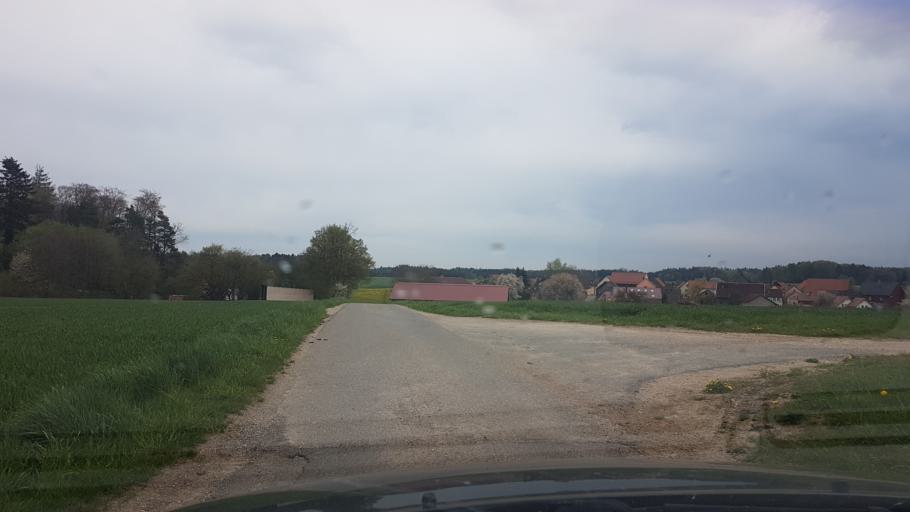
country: DE
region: Bavaria
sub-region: Upper Franconia
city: Wattendorf
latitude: 50.0092
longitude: 11.1543
